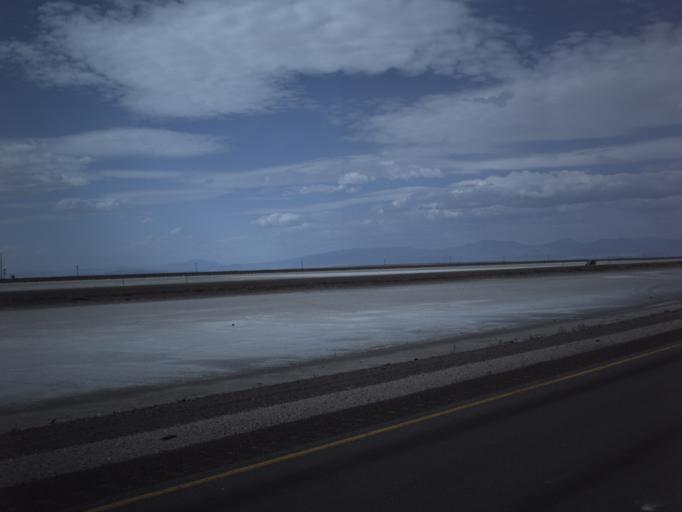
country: US
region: Utah
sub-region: Tooele County
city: Wendover
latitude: 40.7359
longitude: -113.6805
